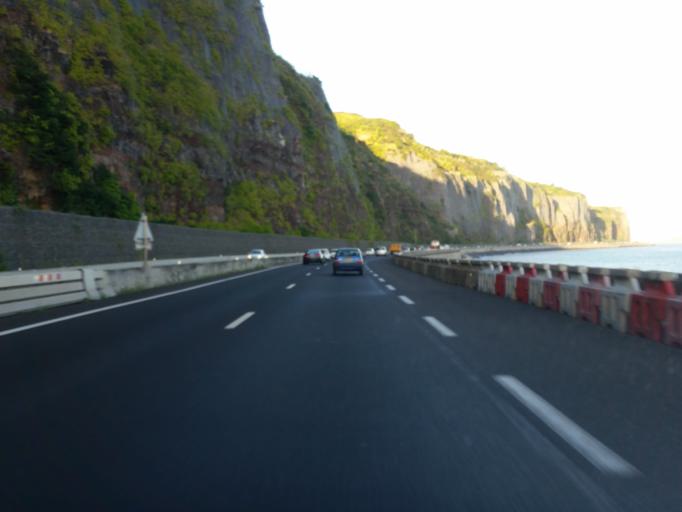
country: RE
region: Reunion
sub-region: Reunion
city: La Possession
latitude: -20.9011
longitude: 55.3677
